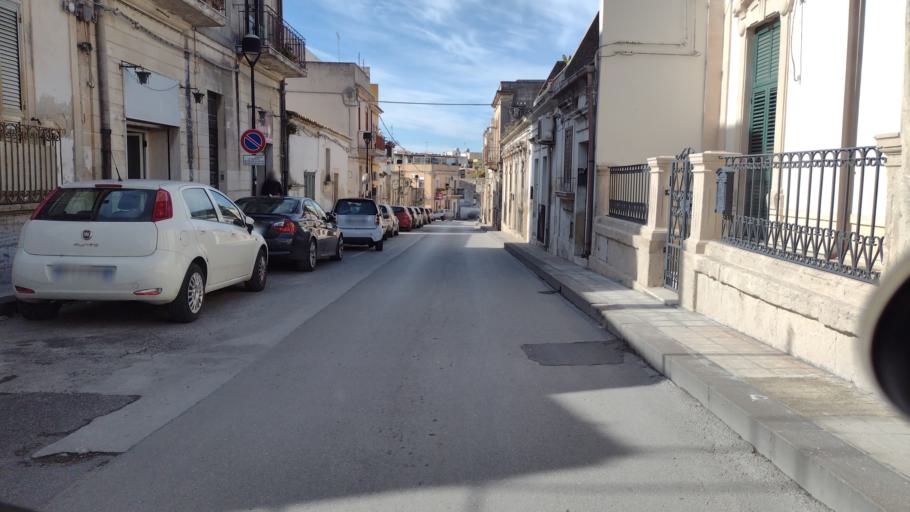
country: IT
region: Sicily
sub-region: Provincia di Siracusa
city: Noto
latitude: 36.8921
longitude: 15.0650
